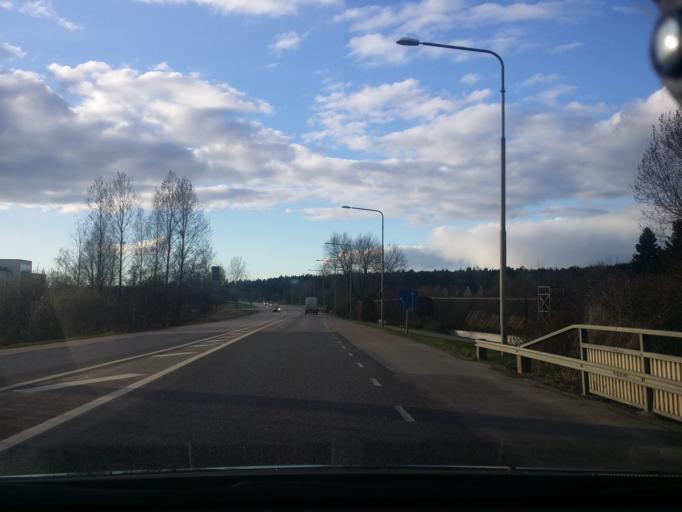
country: SE
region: Vaestmanland
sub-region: Vasteras
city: Vasteras
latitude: 59.5970
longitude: 16.4985
